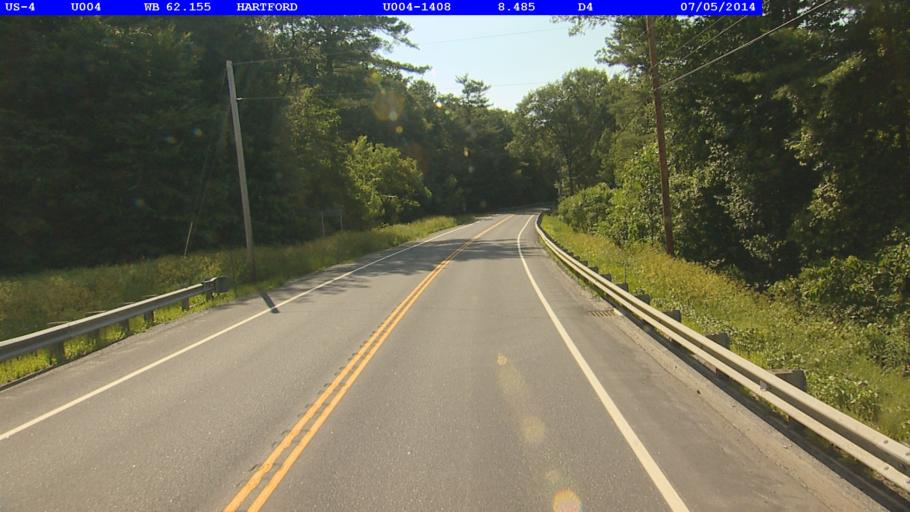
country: US
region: Vermont
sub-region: Windsor County
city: White River Junction
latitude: 43.6574
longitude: -72.3445
